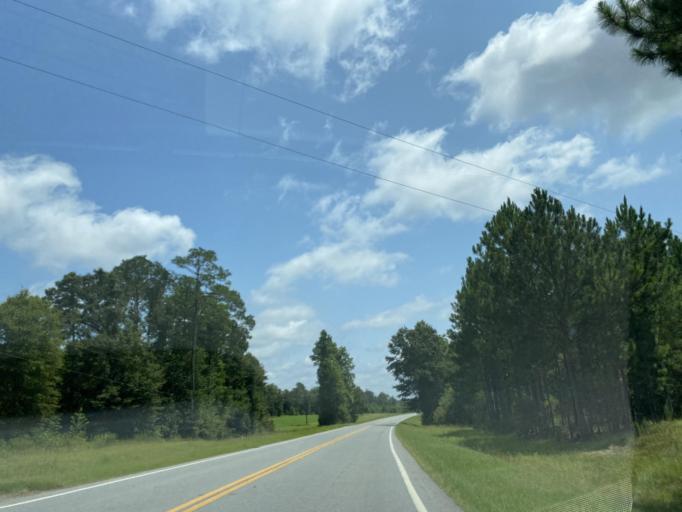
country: US
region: Georgia
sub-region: Telfair County
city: Helena
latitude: 32.0275
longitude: -83.0349
